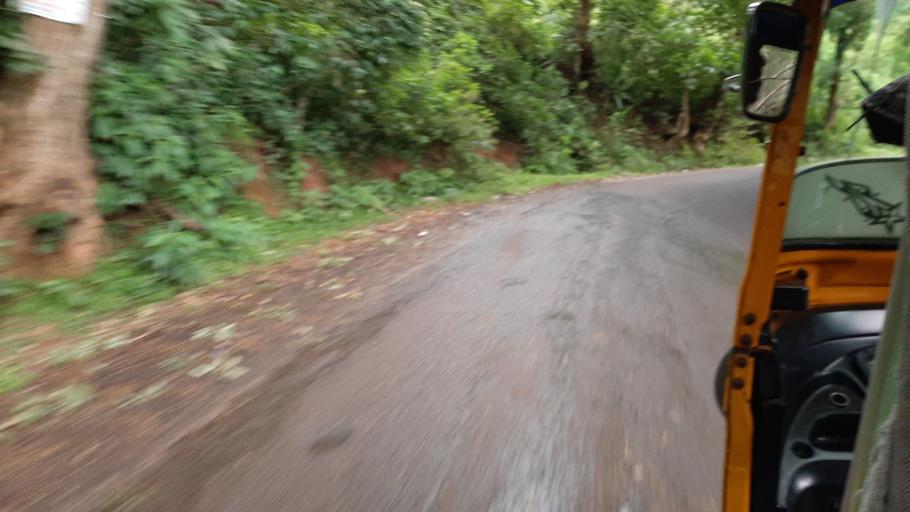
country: IN
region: Andhra Pradesh
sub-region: Vizianagaram District
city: Salur
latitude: 18.2402
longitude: 83.0161
